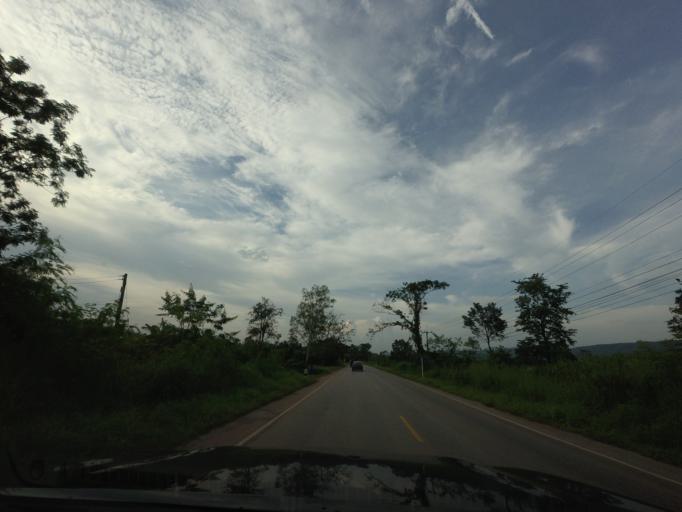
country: TH
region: Changwat Udon Thani
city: Nam Som
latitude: 17.8326
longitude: 102.2616
